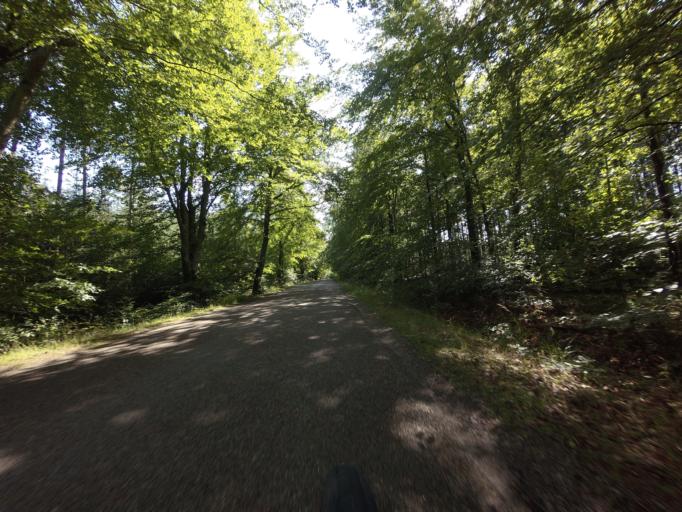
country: DK
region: North Denmark
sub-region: Hjorring Kommune
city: Hirtshals
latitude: 57.5807
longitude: 10.0044
